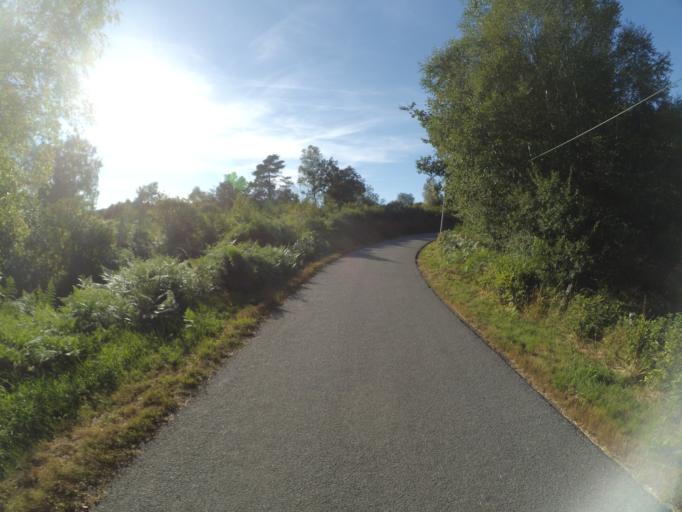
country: FR
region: Limousin
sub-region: Departement de la Creuse
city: Banize
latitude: 45.7660
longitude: 2.0196
